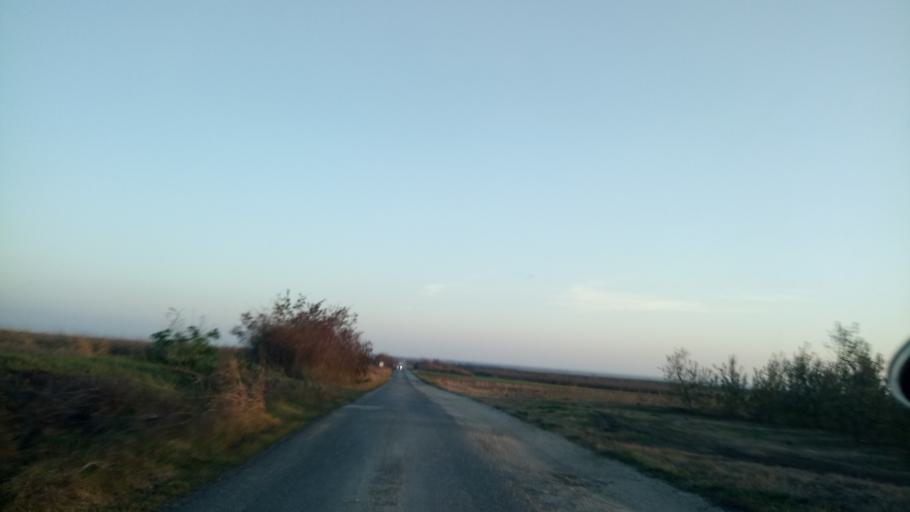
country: RS
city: Novi Slankamen
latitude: 45.1096
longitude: 20.2791
